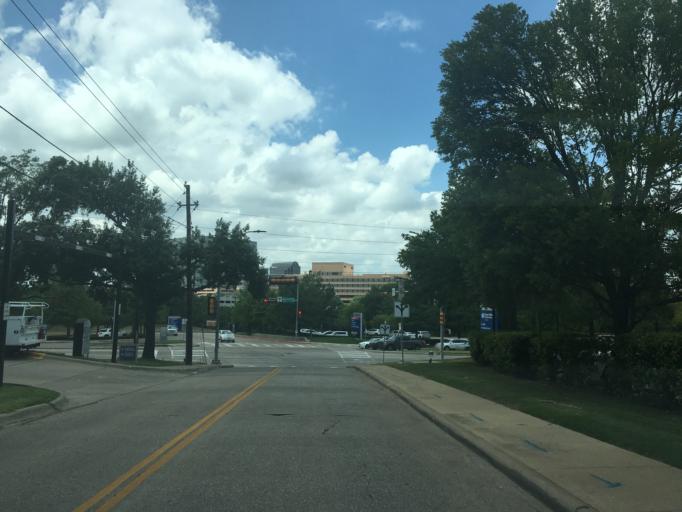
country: US
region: Texas
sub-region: Dallas County
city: University Park
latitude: 32.8771
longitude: -96.7605
